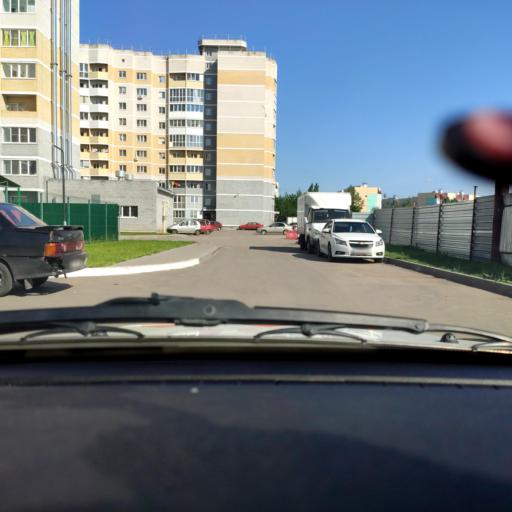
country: RU
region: Voronezj
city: Novaya Usman'
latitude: 51.6121
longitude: 39.3678
